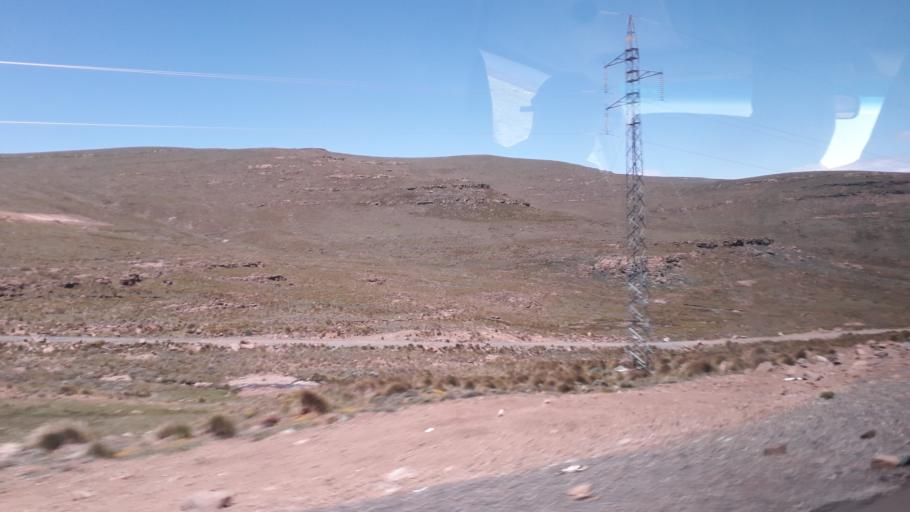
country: ZA
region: Orange Free State
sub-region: Thabo Mofutsanyana District Municipality
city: Phuthaditjhaba
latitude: -28.8081
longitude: 28.7059
